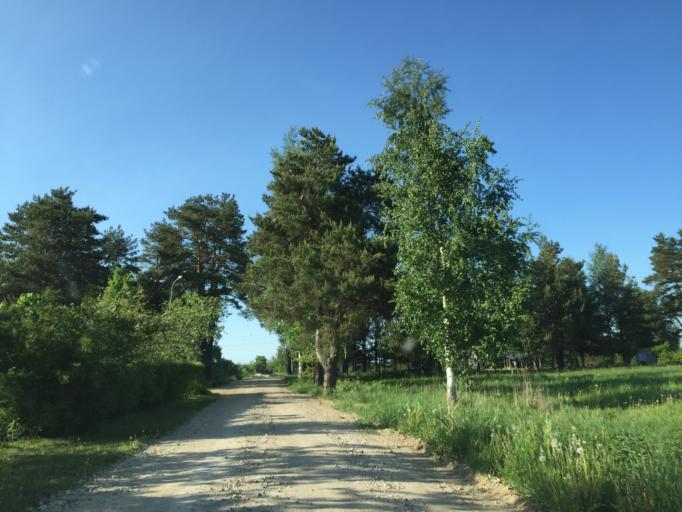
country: LV
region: Kekava
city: Kekava
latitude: 56.8247
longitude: 24.2624
